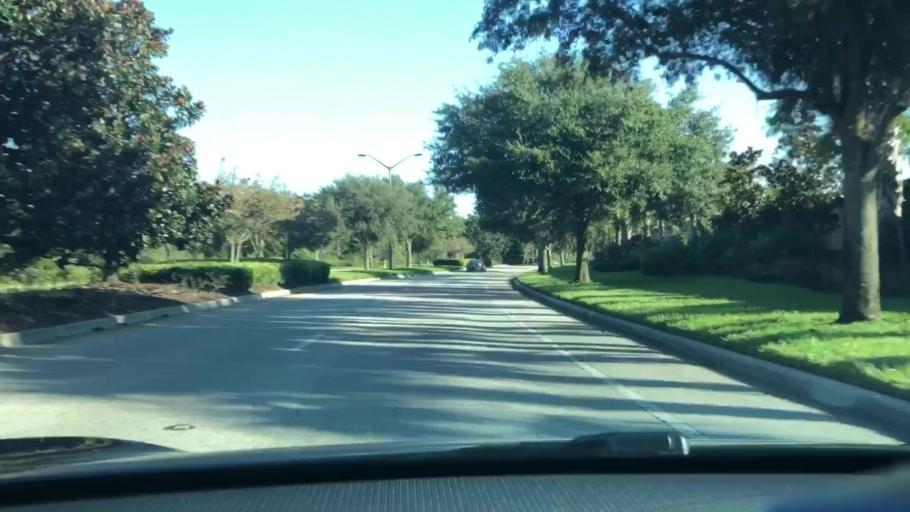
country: US
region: Florida
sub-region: Orange County
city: Meadow Woods
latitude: 28.3914
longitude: -81.2761
